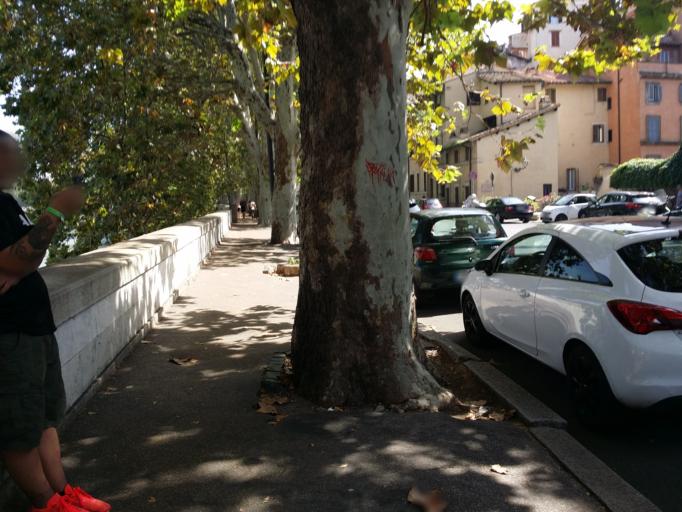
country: VA
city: Vatican City
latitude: 41.9014
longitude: 12.4679
